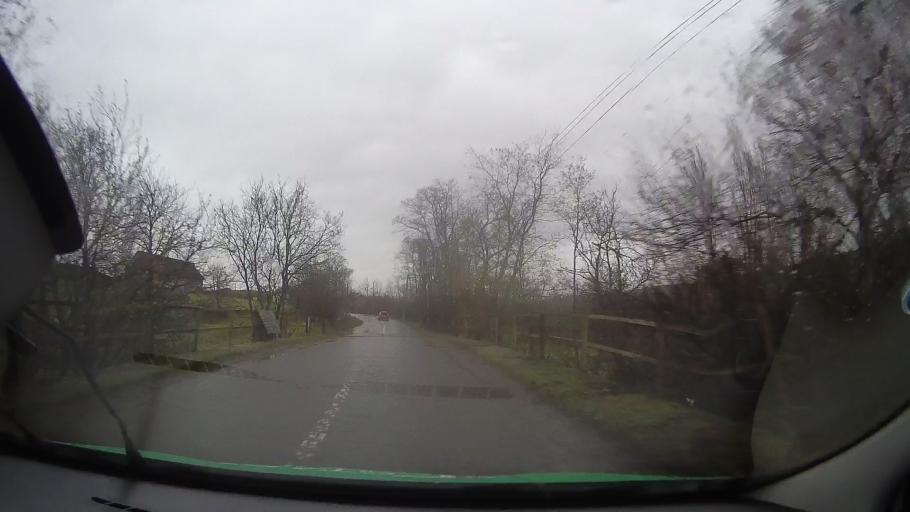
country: RO
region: Mures
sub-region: Comuna Vatava
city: Vatava
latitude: 46.9262
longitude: 24.7705
